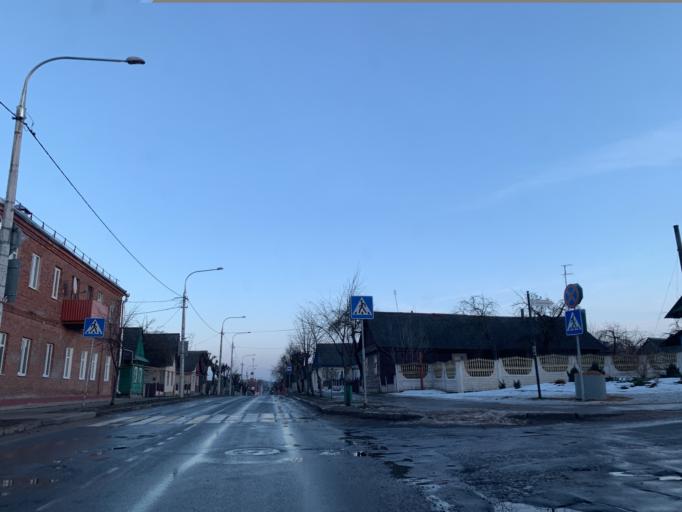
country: BY
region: Minsk
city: Nyasvizh
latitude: 53.2236
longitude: 26.6743
